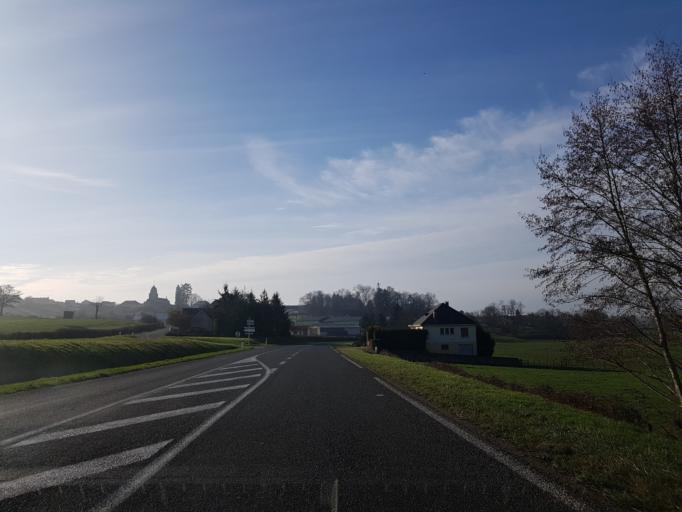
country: FR
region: Bourgogne
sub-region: Departement de Saone-et-Loire
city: La Motte-Saint-Jean
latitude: 46.5941
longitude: 3.9401
